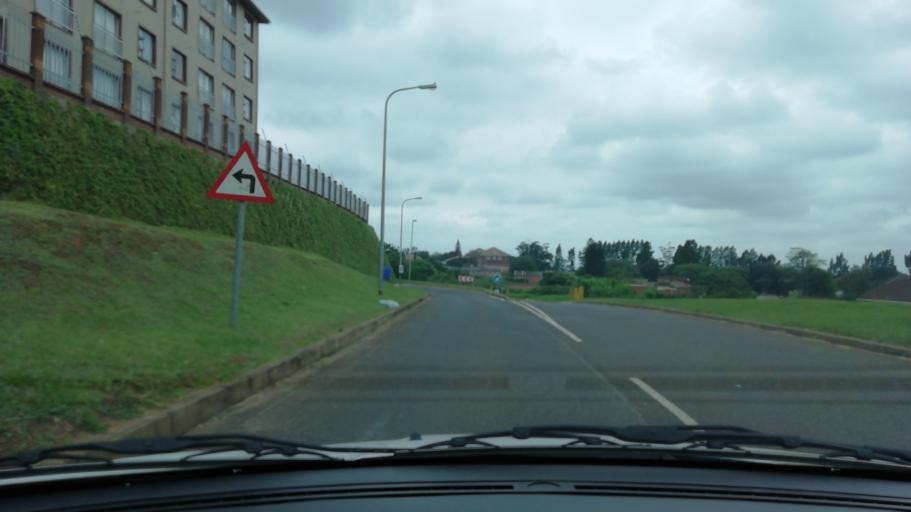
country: ZA
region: KwaZulu-Natal
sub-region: uThungulu District Municipality
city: Empangeni
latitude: -28.7479
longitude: 31.8890
